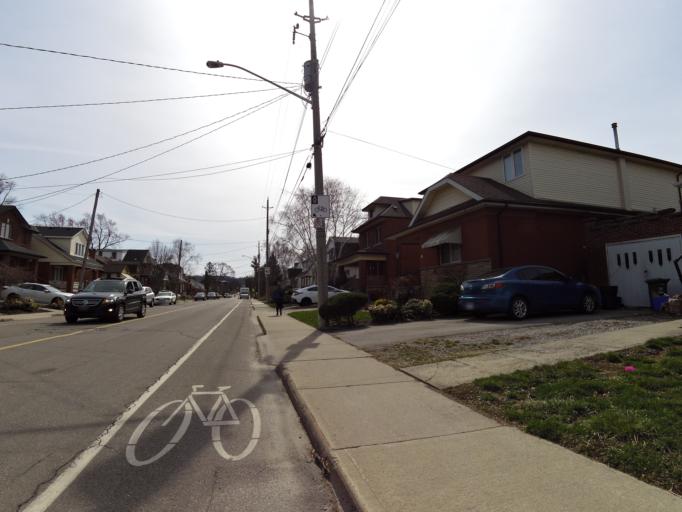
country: CA
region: Ontario
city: Hamilton
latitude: 43.2656
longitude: -79.8997
